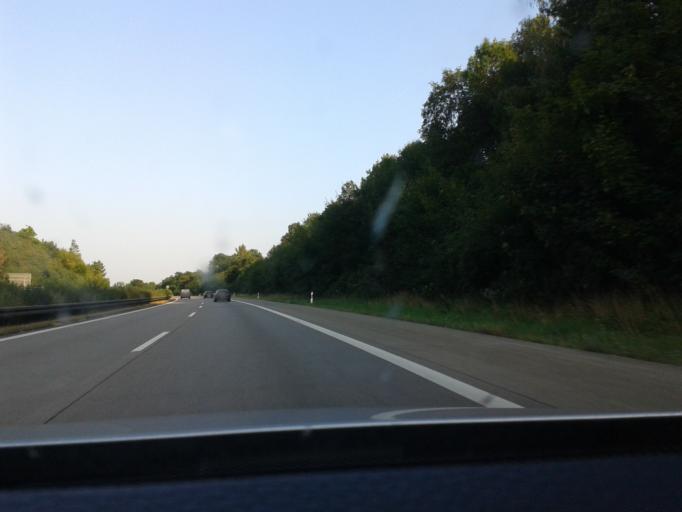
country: DE
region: Saxony
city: Nerchau
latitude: 51.2536
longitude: 12.7928
